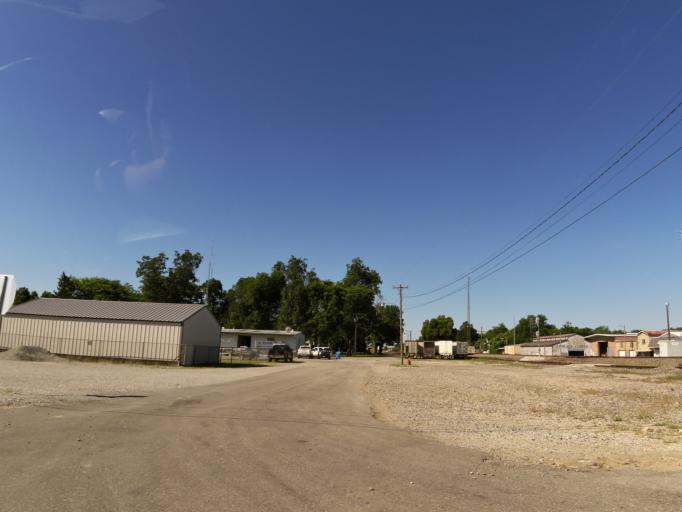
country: US
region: Arkansas
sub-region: Clay County
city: Corning
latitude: 36.4078
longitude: -90.5796
